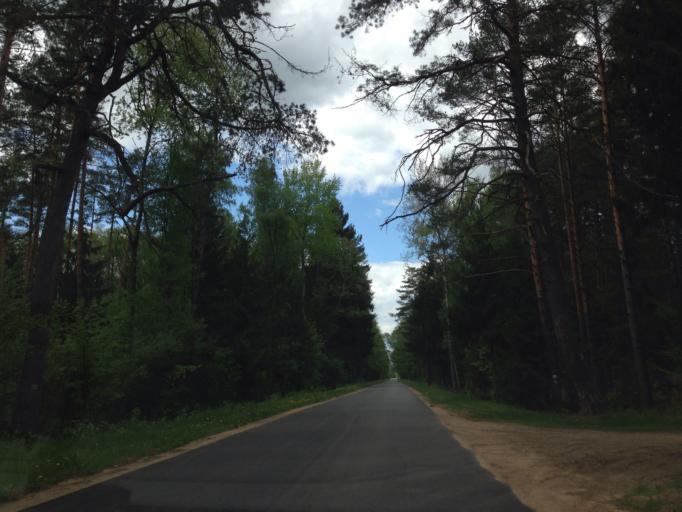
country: PL
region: Podlasie
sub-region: Powiat moniecki
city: Goniadz
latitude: 53.3640
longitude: 22.5971
